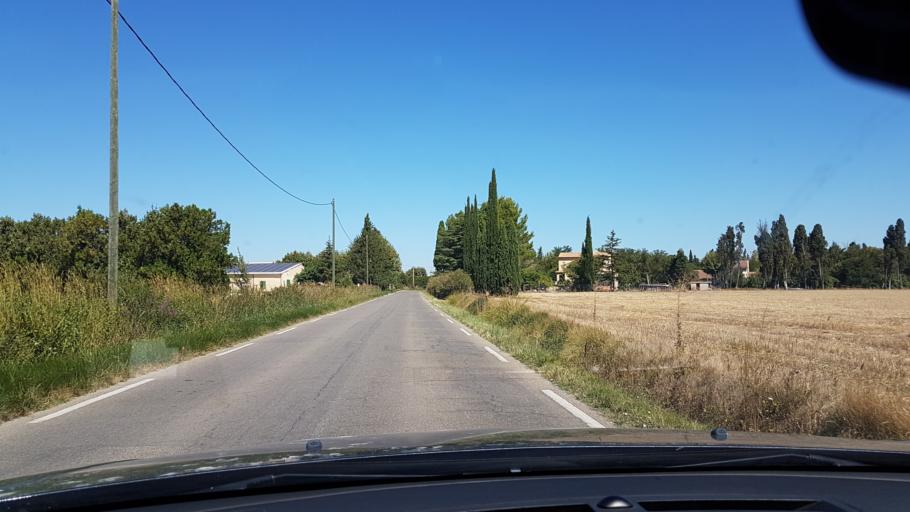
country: FR
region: Provence-Alpes-Cote d'Azur
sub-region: Departement des Bouches-du-Rhone
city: Molleges
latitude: 43.7997
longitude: 4.9523
